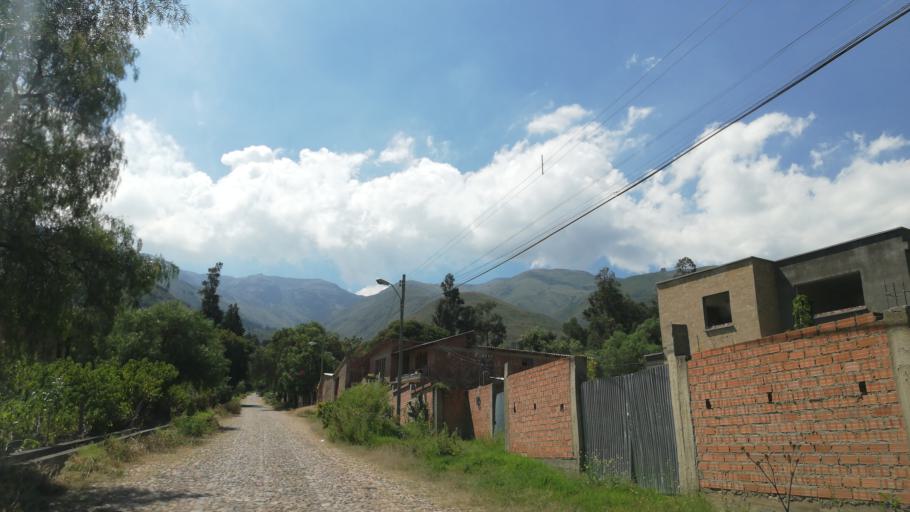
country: BO
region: Cochabamba
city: Cochabamba
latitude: -17.3262
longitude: -66.2139
